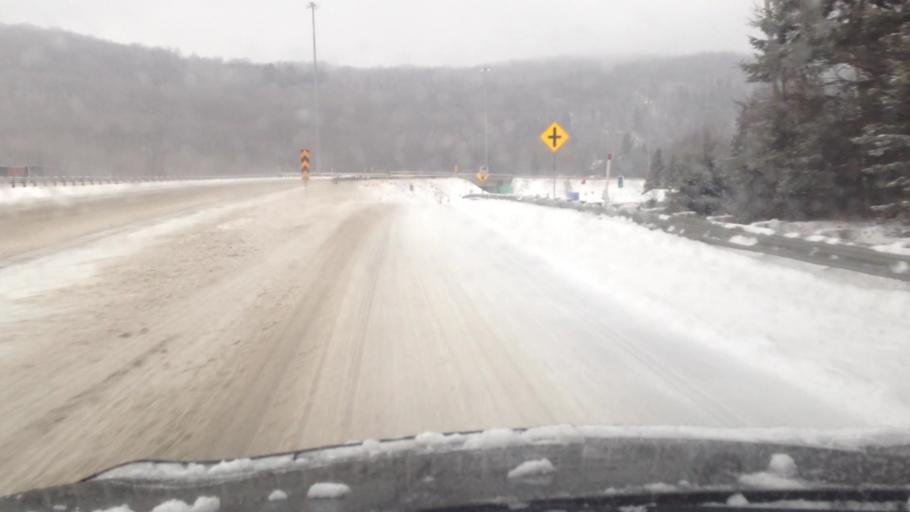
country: CA
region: Quebec
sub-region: Laurentides
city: Mont-Tremblant
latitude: 46.1142
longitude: -74.6033
